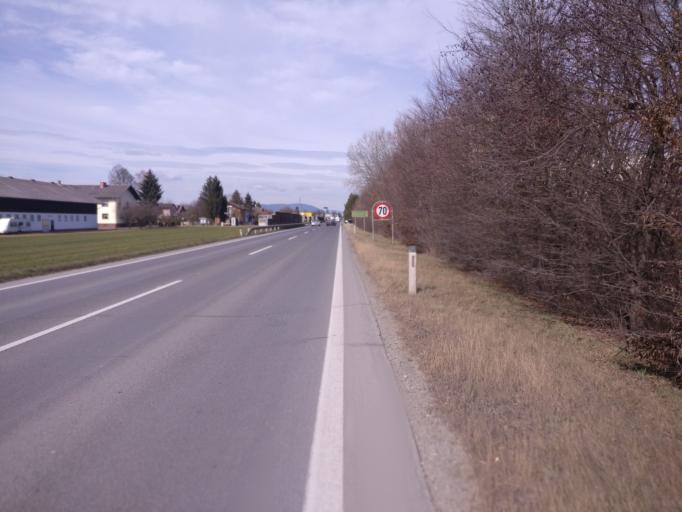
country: AT
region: Styria
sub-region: Politischer Bezirk Graz-Umgebung
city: Gossendorf
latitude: 46.9818
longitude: 15.4536
